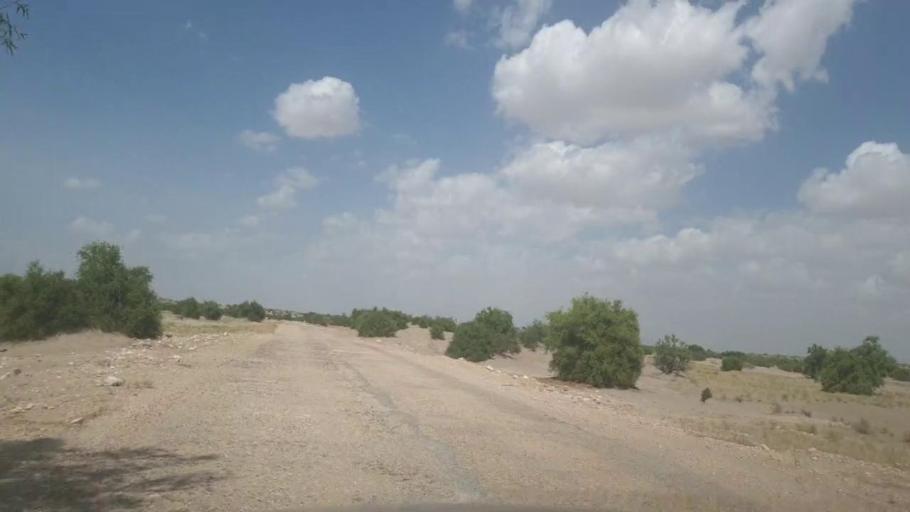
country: PK
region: Sindh
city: Kot Diji
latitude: 27.2641
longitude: 69.1760
